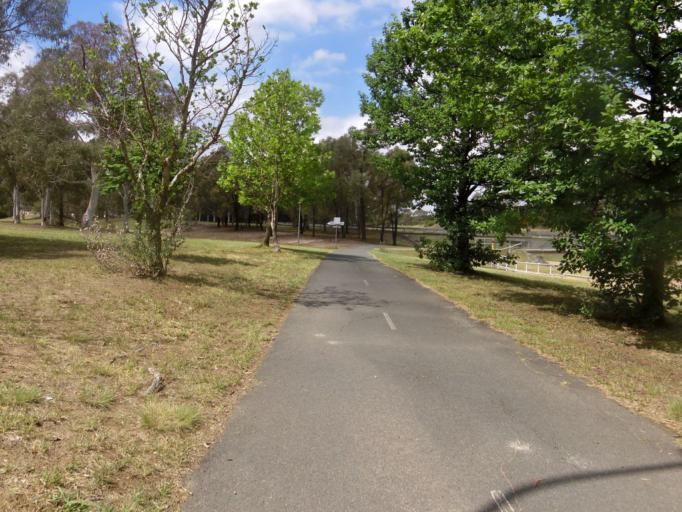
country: AU
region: Australian Capital Territory
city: Macarthur
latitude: -35.4161
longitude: 149.1131
